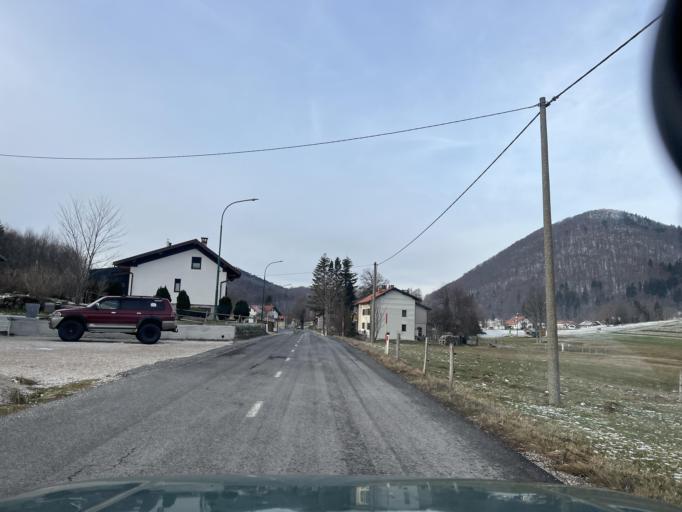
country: SI
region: Nova Gorica
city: Sempas
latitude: 46.0093
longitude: 13.7943
